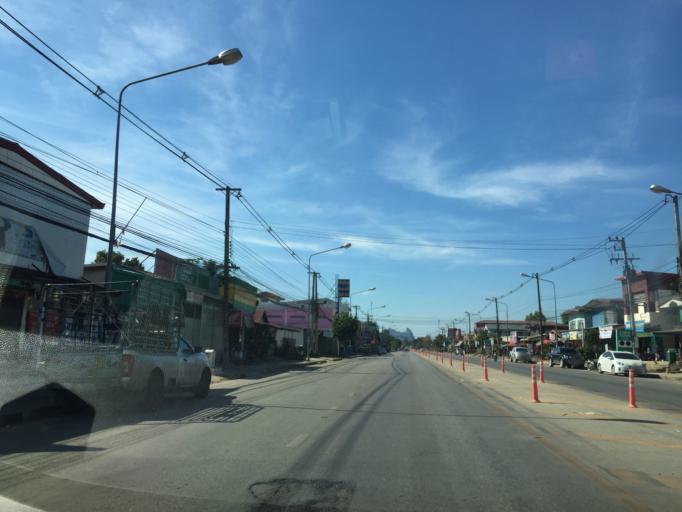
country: TH
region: Changwat Nong Bua Lamphu
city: Na Wang
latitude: 17.3231
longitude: 102.0838
